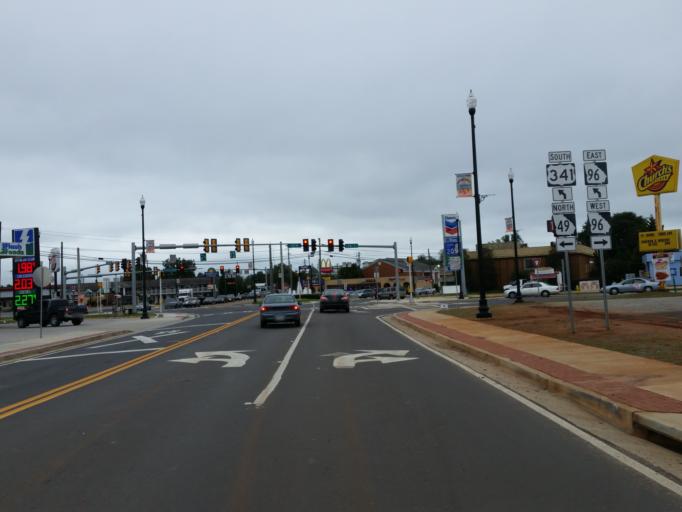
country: US
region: Georgia
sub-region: Peach County
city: Fort Valley
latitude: 32.5594
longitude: -83.8838
